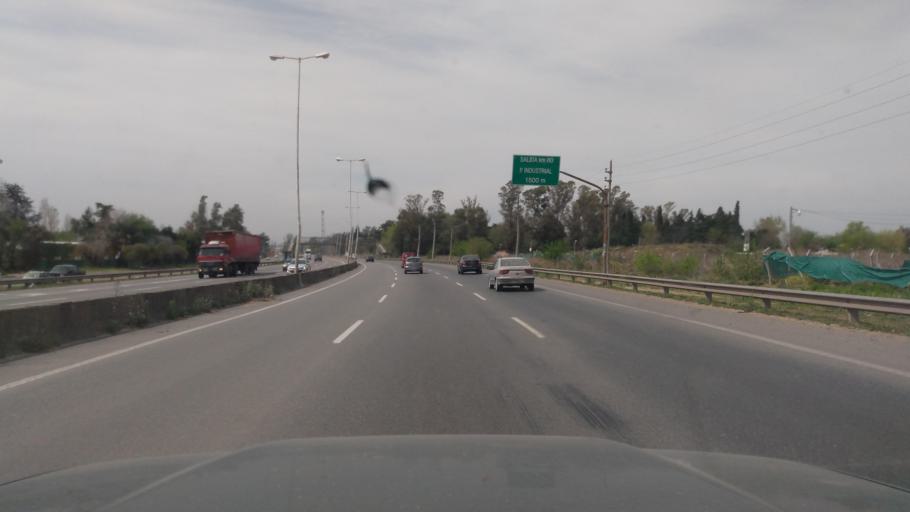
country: AR
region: Buenos Aires
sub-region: Partido de Pilar
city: Pilar
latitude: -34.4355
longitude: -58.9871
